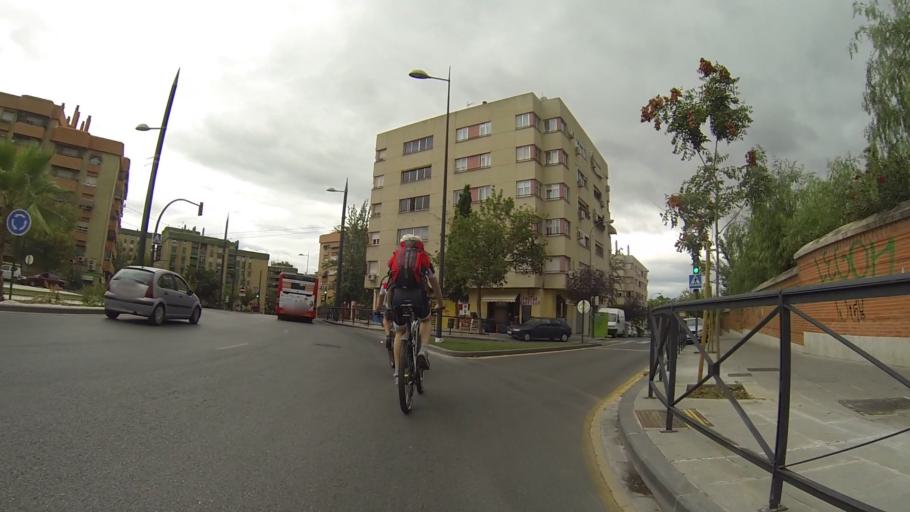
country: ES
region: Andalusia
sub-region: Provincia de Granada
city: Granada
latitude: 37.1912
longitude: -3.6152
